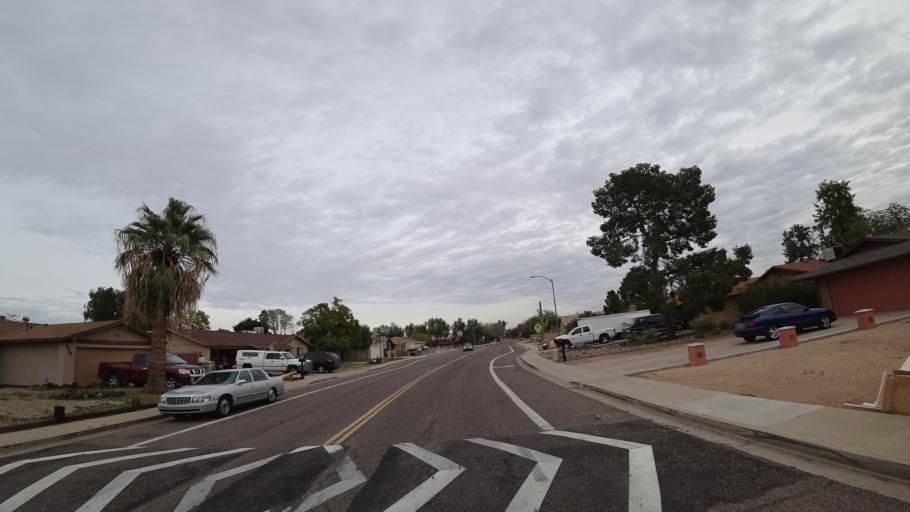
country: US
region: Arizona
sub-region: Maricopa County
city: Peoria
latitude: 33.6471
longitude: -112.1791
